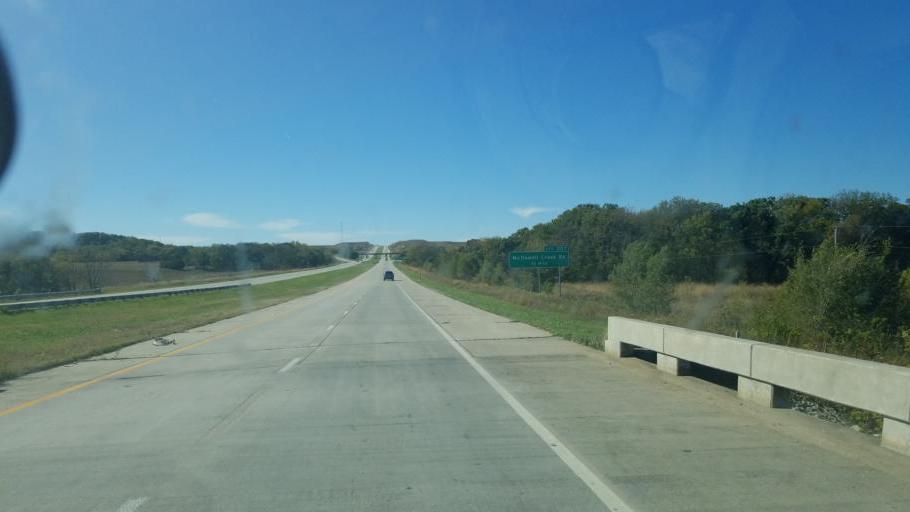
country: US
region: Kansas
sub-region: Riley County
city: Ogden
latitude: 39.0673
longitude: -96.6451
